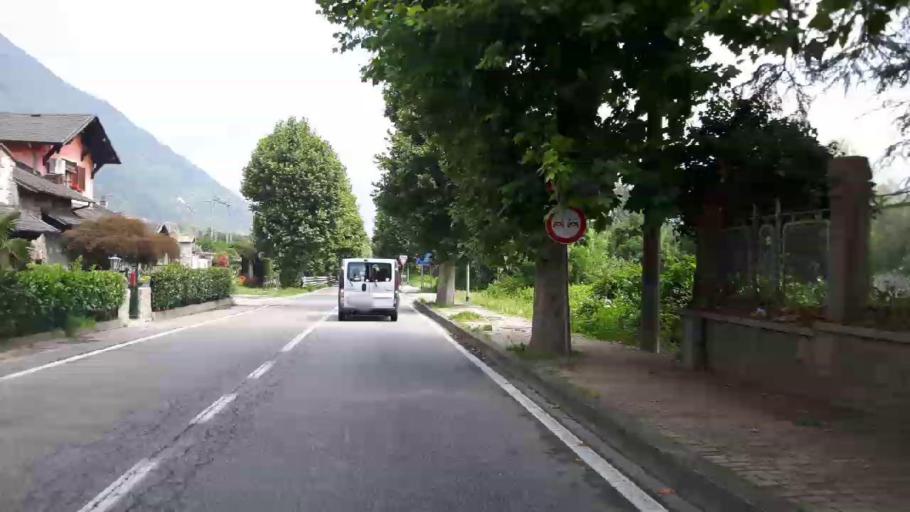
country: IT
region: Piedmont
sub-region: Provincia Verbano-Cusio-Ossola
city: Gravellona Toce
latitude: 45.9344
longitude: 8.4300
